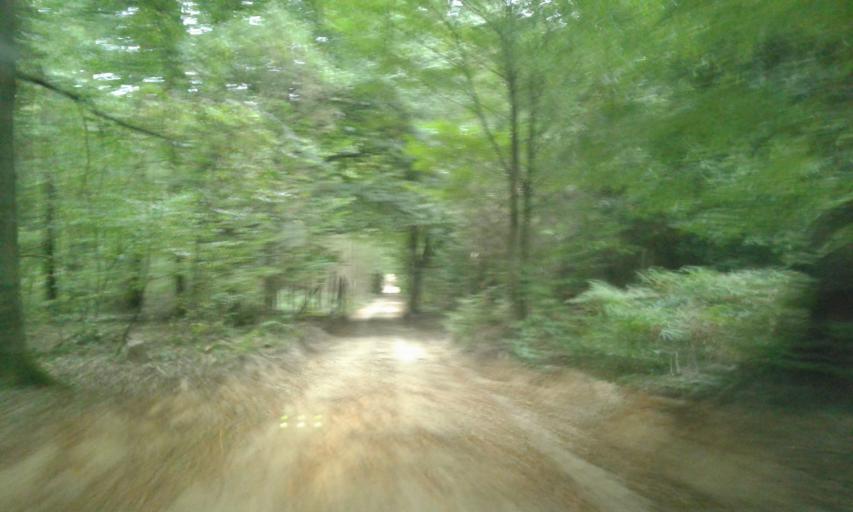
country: PL
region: West Pomeranian Voivodeship
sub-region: Powiat stargardzki
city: Dolice
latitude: 53.1793
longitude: 15.2490
